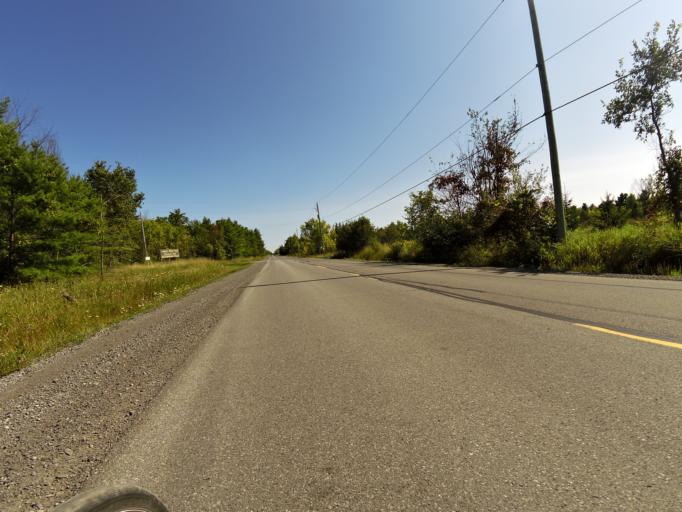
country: CA
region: Ontario
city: Bells Corners
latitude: 45.4333
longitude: -75.9633
